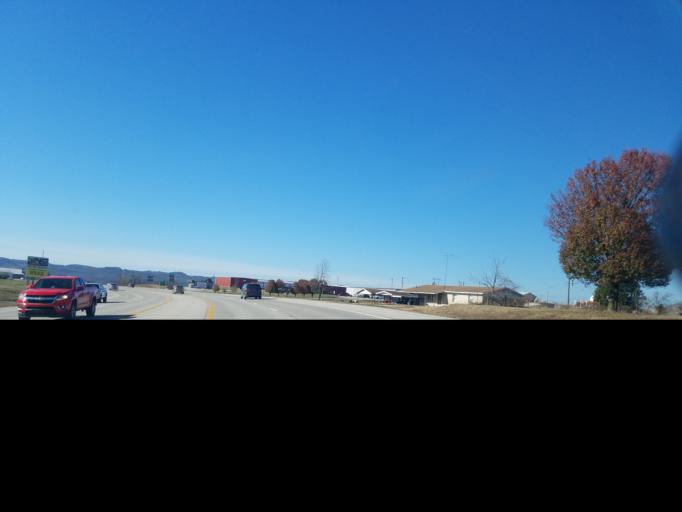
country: US
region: Arkansas
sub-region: Carroll County
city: Berryville
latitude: 36.3898
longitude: -93.6175
